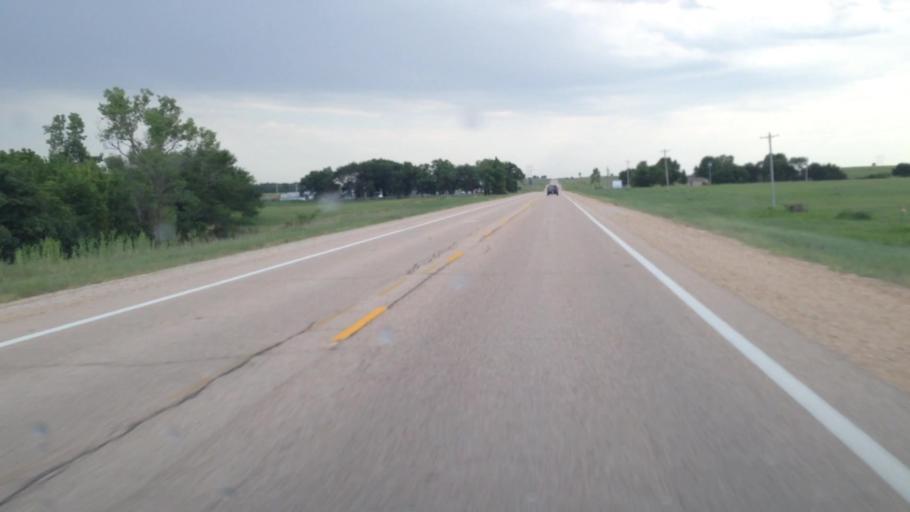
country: US
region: Kansas
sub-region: Coffey County
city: Burlington
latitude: 38.1685
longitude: -95.7389
